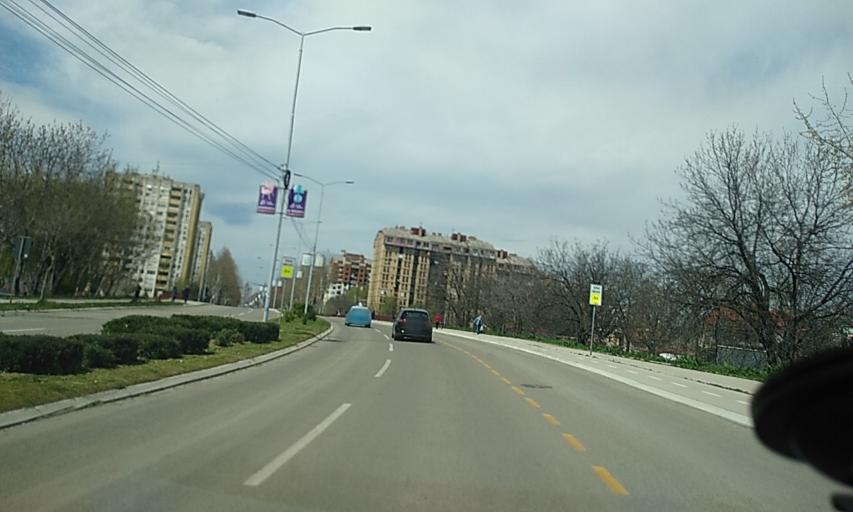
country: RS
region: Central Serbia
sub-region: Nisavski Okrug
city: Nis
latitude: 43.3156
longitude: 21.9270
